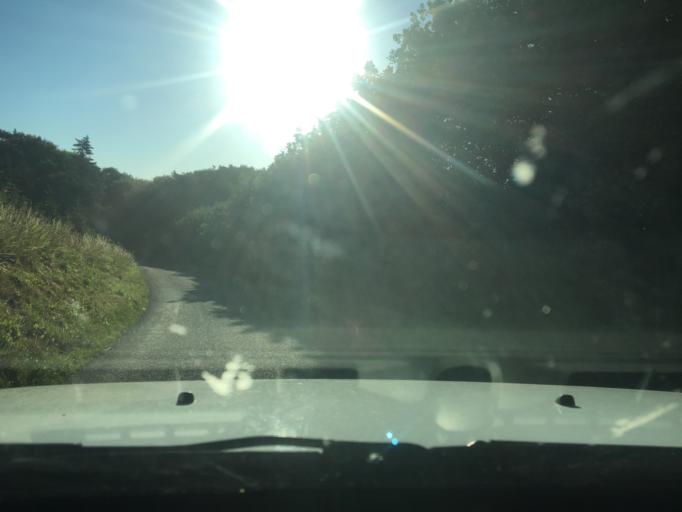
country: DK
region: Central Jutland
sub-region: Favrskov Kommune
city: Hadsten
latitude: 56.3949
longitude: 10.0771
